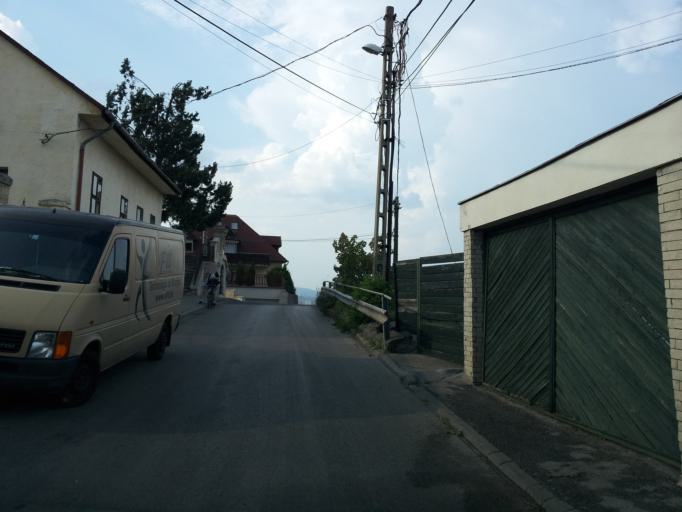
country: HU
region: Budapest
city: Budapest XXII. keruelet
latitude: 47.4260
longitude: 19.0366
